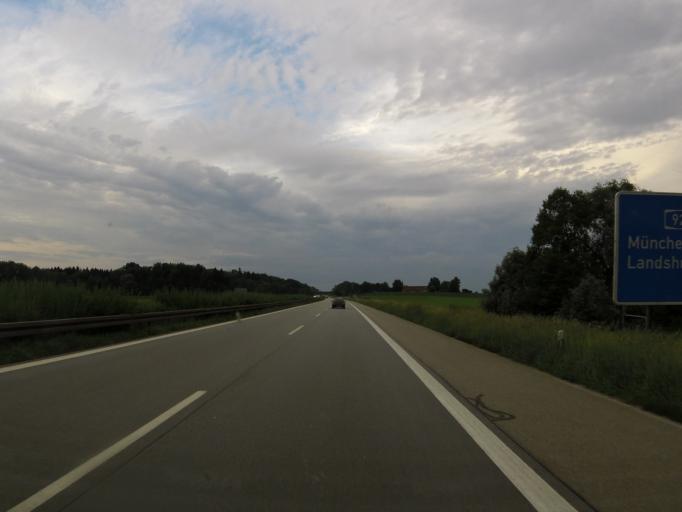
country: DE
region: Bavaria
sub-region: Lower Bavaria
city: Deggendorf
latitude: 48.8101
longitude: 12.9283
